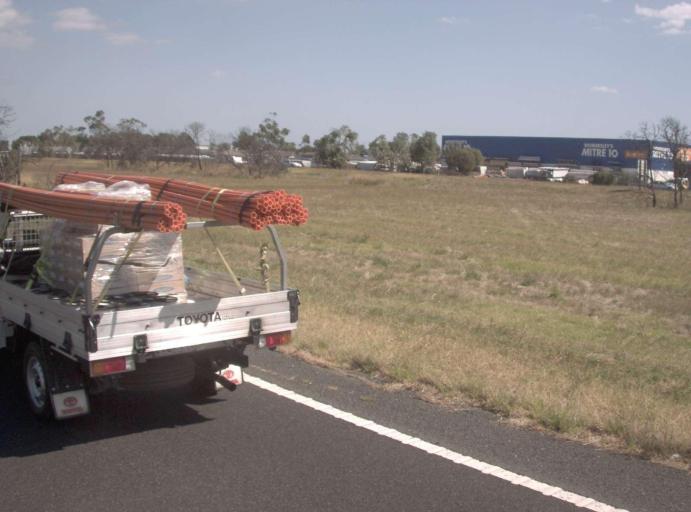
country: AU
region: Victoria
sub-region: Kingston
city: Chelsea Heights
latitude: -38.0268
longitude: 145.1354
